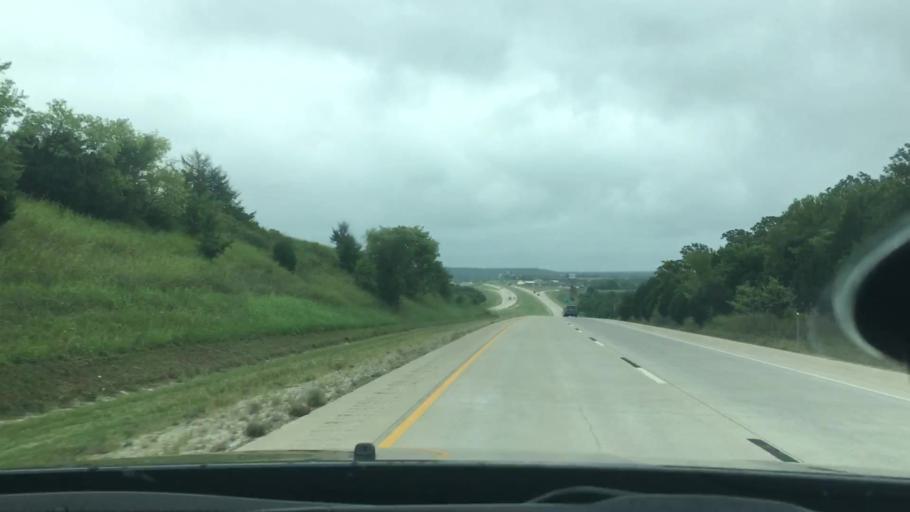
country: US
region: Oklahoma
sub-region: Okmulgee County
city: Henryetta
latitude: 35.4323
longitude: -96.0323
